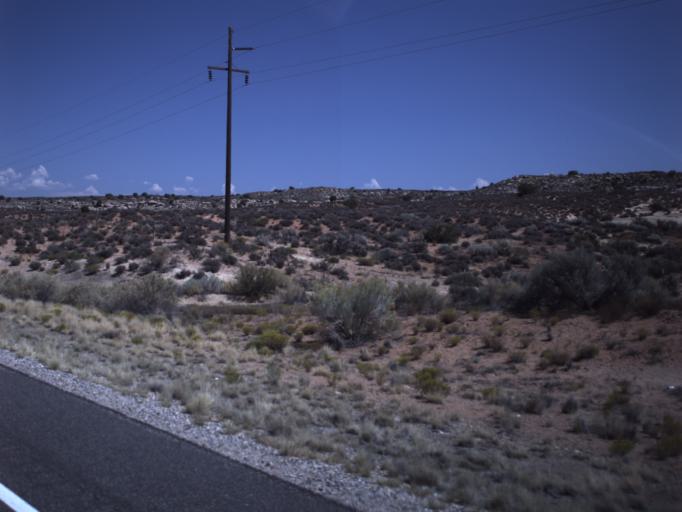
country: US
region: Utah
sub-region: San Juan County
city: Blanding
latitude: 37.3693
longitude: -109.5070
